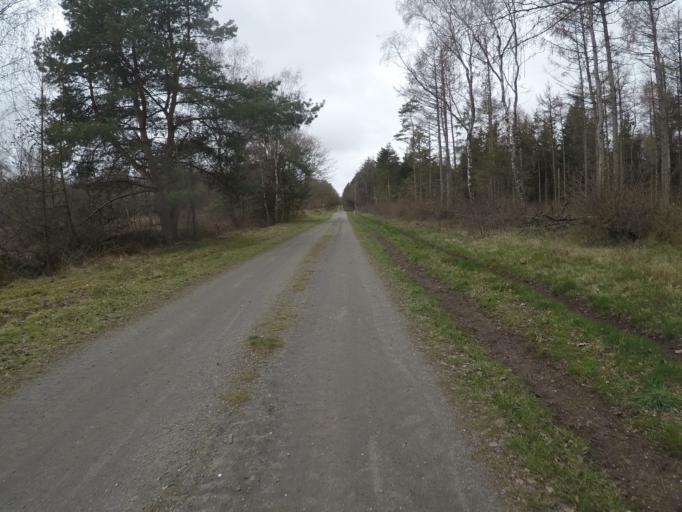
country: DE
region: Lower Saxony
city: Nordholz
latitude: 53.8287
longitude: 8.6093
